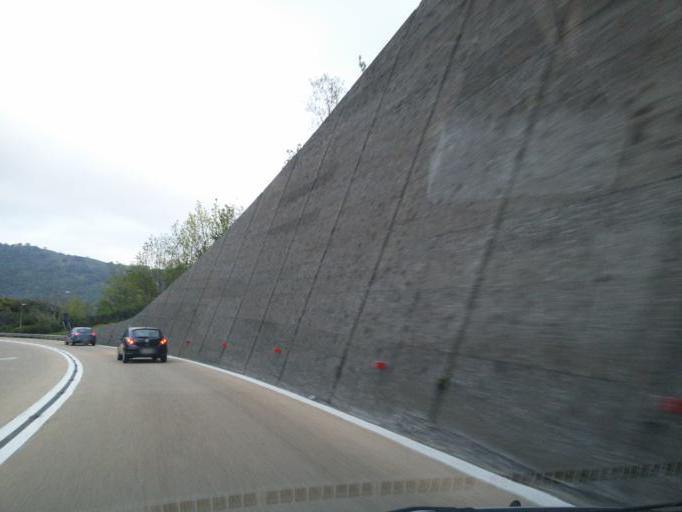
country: IT
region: Liguria
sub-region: Provincia di Genova
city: Genoa
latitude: 44.4331
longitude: 8.9418
